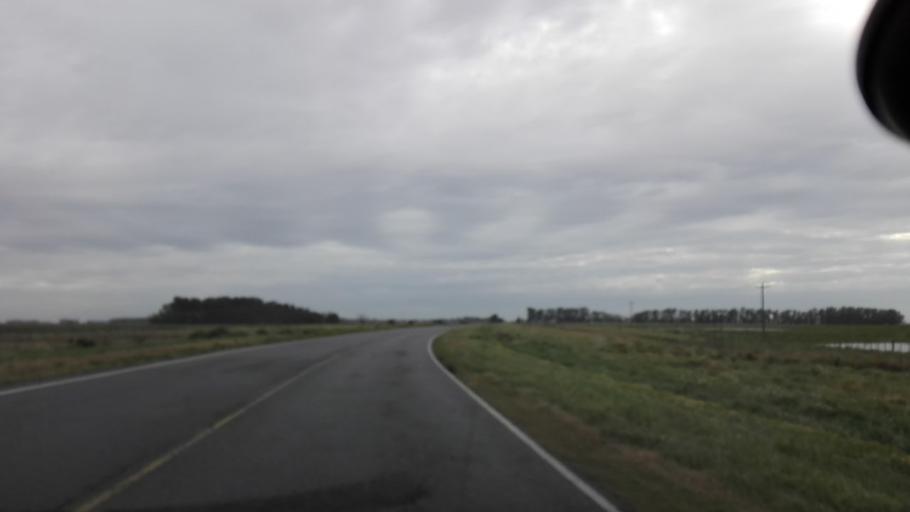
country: AR
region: Buenos Aires
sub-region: Partido de Rauch
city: Rauch
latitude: -36.6397
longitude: -59.0659
